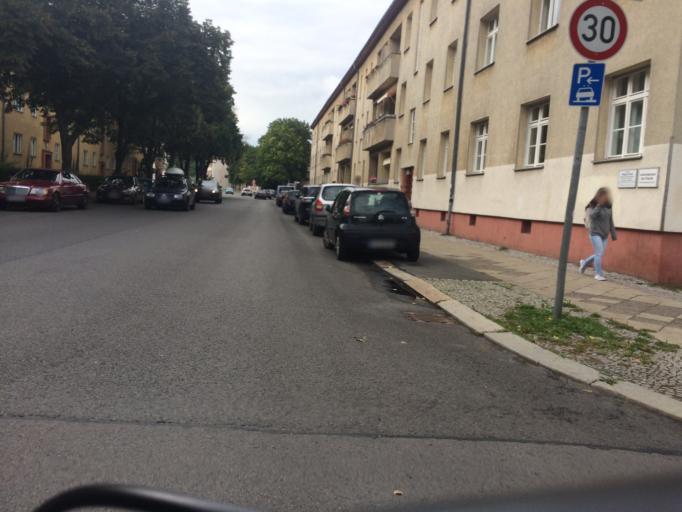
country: DE
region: Berlin
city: Alt-Hohenschoenhausen
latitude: 52.5405
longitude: 13.4950
